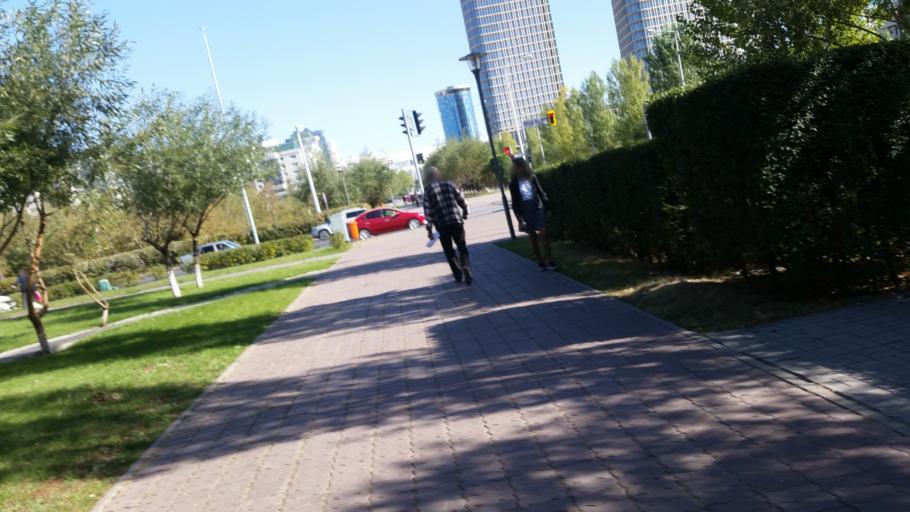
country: KZ
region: Astana Qalasy
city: Astana
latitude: 51.1265
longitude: 71.4272
